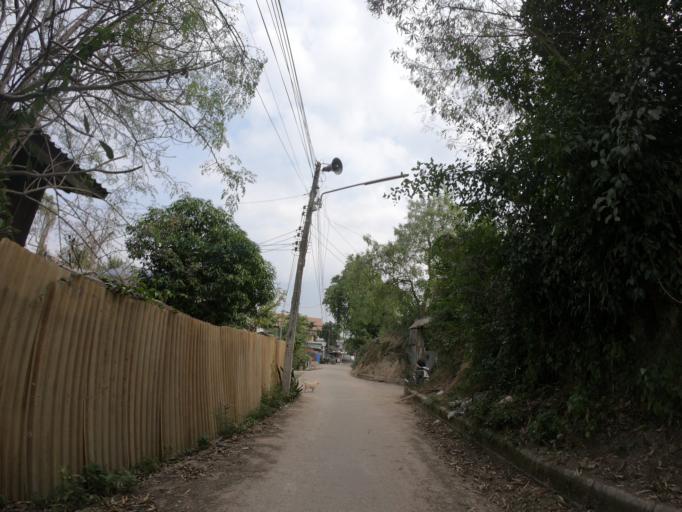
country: TH
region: Chiang Mai
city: Chiang Mai
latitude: 18.7733
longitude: 98.9864
